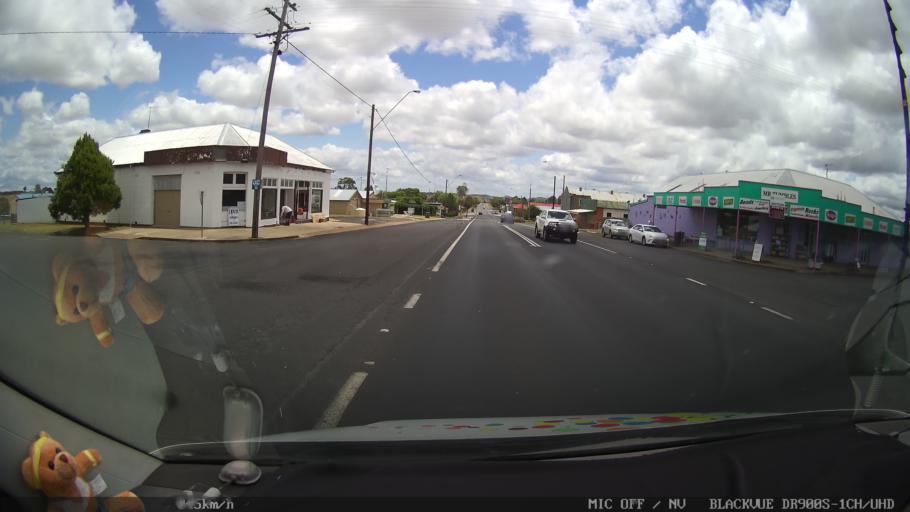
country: AU
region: New South Wales
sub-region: Glen Innes Severn
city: Glen Innes
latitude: -29.4426
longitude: 151.8460
